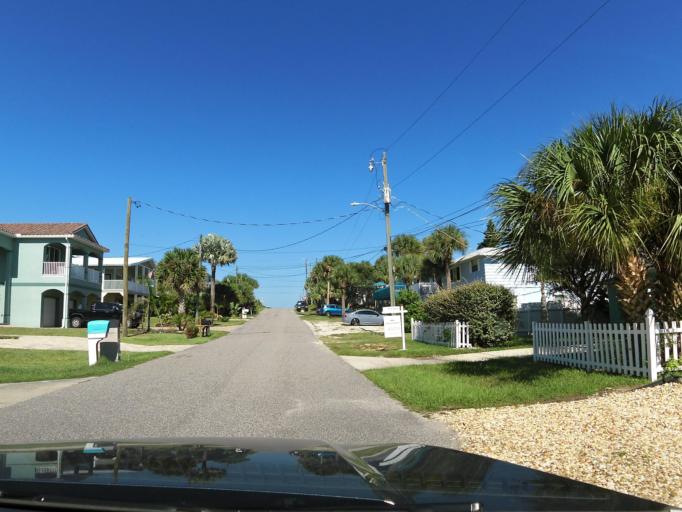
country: US
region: Florida
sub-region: Flagler County
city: Flagler Beach
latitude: 29.4473
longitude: -81.1139
